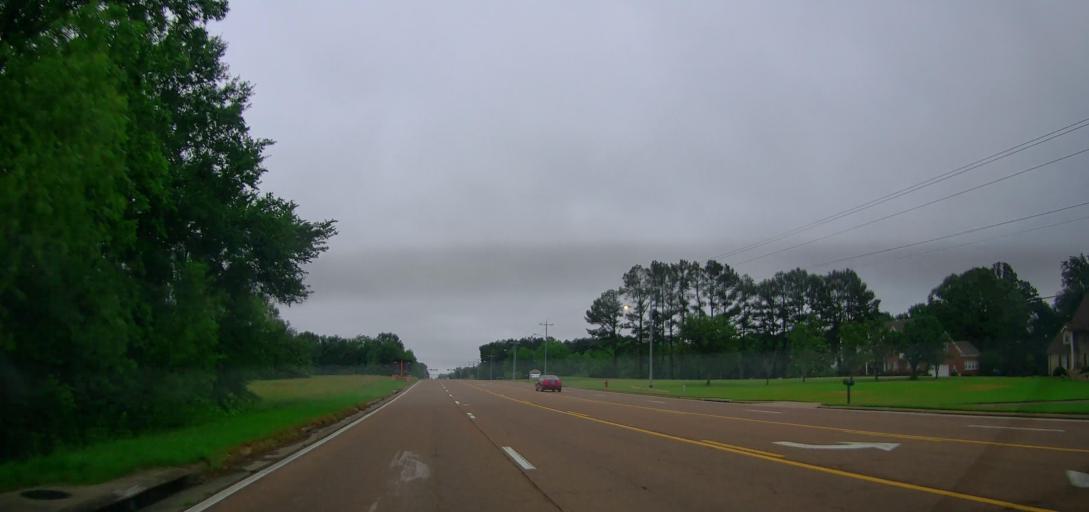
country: US
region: Mississippi
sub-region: De Soto County
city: Olive Branch
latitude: 34.9804
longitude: -89.8307
